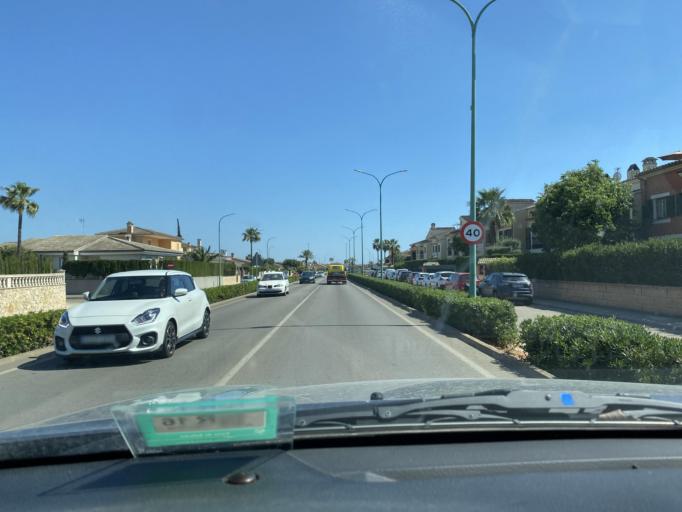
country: ES
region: Balearic Islands
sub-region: Illes Balears
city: Palma
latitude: 39.6134
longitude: 2.6838
